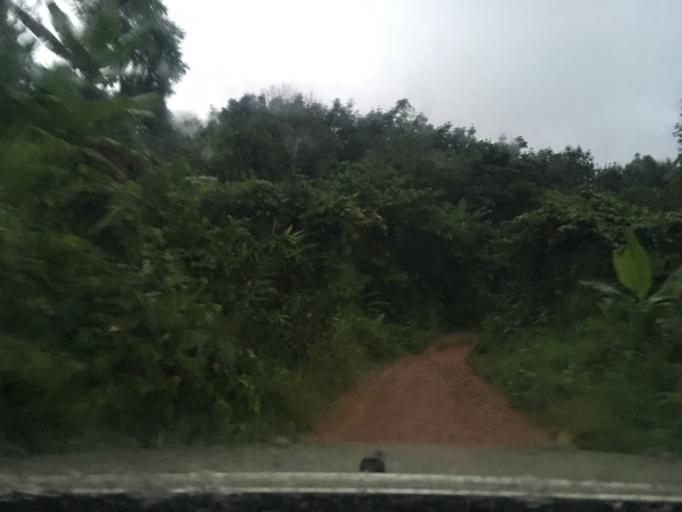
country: LA
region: Oudomxai
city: Muang La
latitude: 21.2462
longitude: 101.9333
